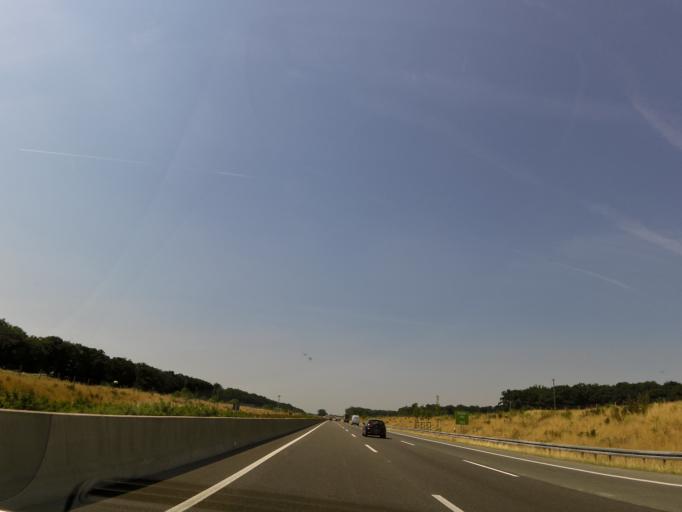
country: DE
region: North Rhine-Westphalia
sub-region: Regierungsbezirk Koln
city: Merzenich
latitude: 50.8535
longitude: 6.5493
